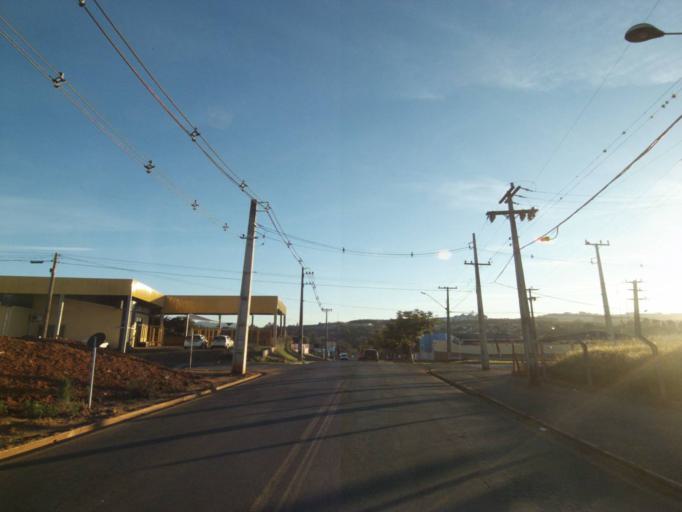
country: BR
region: Parana
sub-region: Tibagi
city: Tibagi
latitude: -24.5103
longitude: -50.4171
